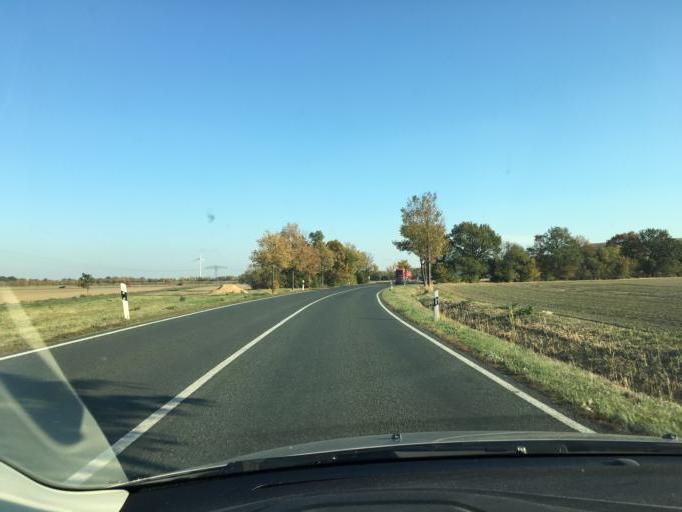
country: DE
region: Saxony
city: Rackwitz
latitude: 51.4185
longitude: 12.3922
